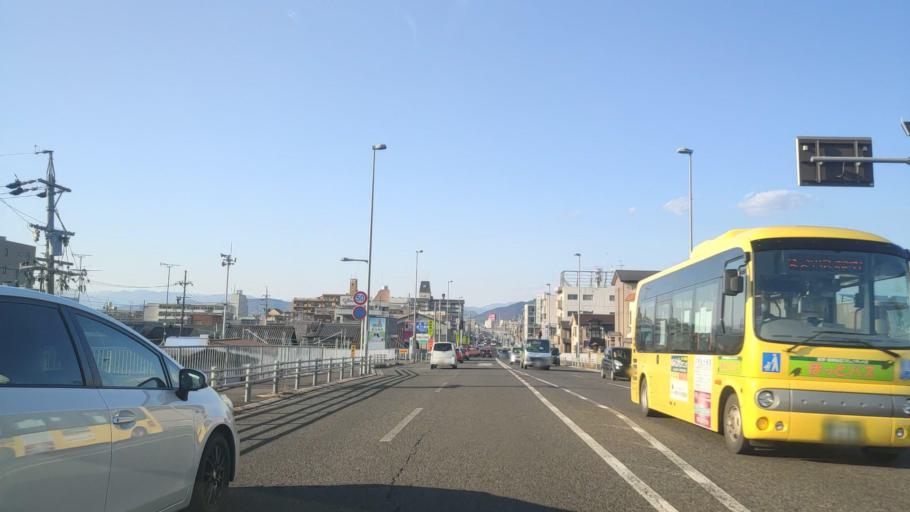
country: JP
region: Gifu
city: Gifu-shi
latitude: 35.4321
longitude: 136.7497
